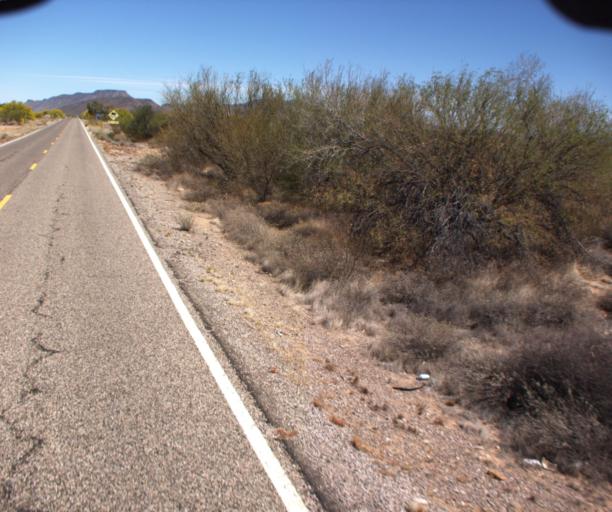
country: US
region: Arizona
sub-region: Pima County
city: Ajo
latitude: 32.2365
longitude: -112.7512
